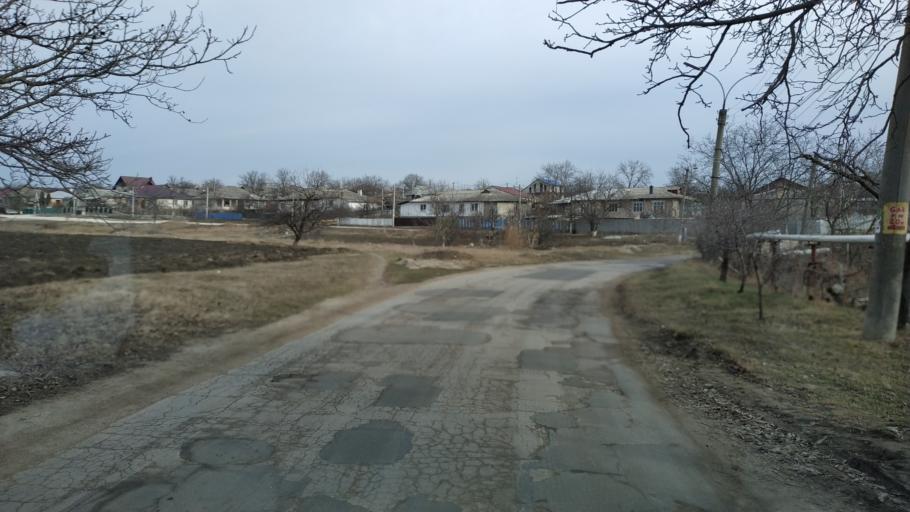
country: MD
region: Chisinau
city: Vatra
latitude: 47.0947
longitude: 28.7618
